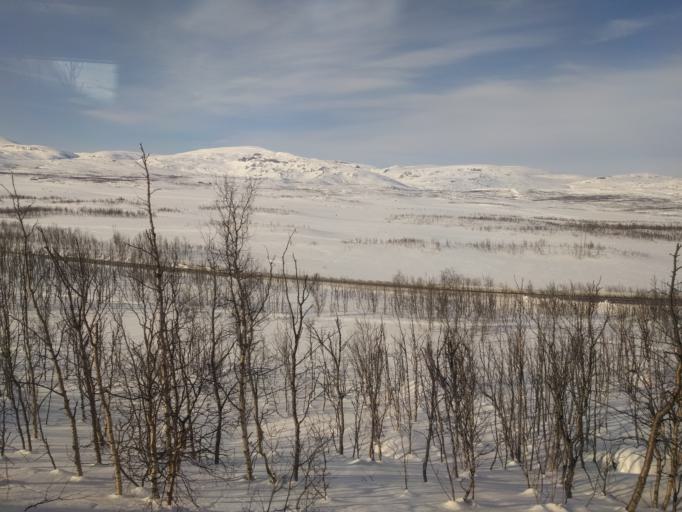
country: NO
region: Troms
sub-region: Bardu
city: Setermoen
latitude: 68.4250
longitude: 18.3815
